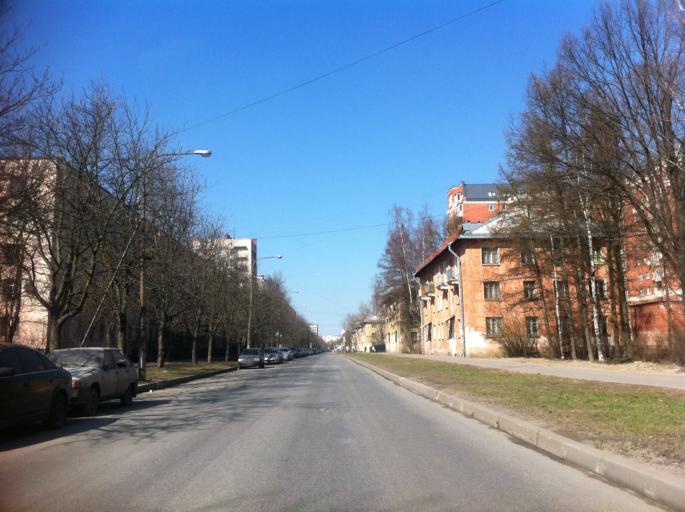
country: RU
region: St.-Petersburg
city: Dachnoye
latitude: 59.8364
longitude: 30.2540
